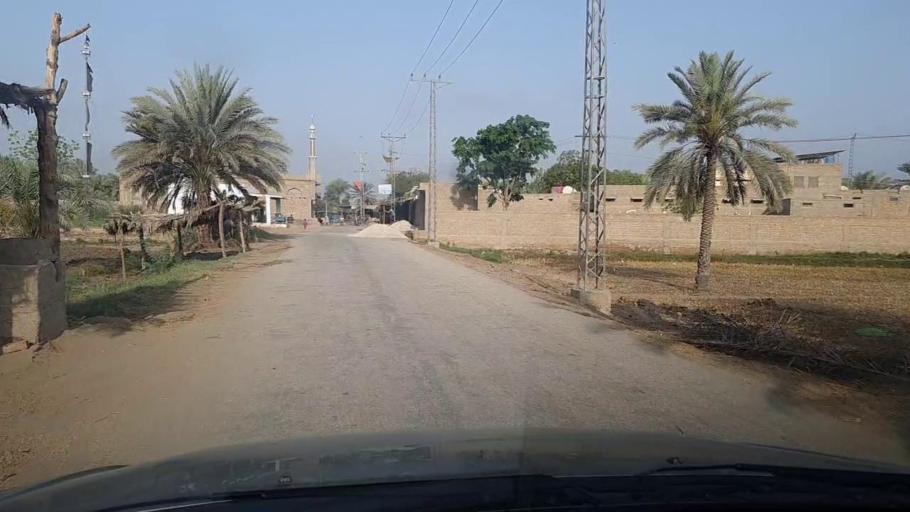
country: PK
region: Sindh
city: Pir jo Goth
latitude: 27.5712
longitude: 68.6136
